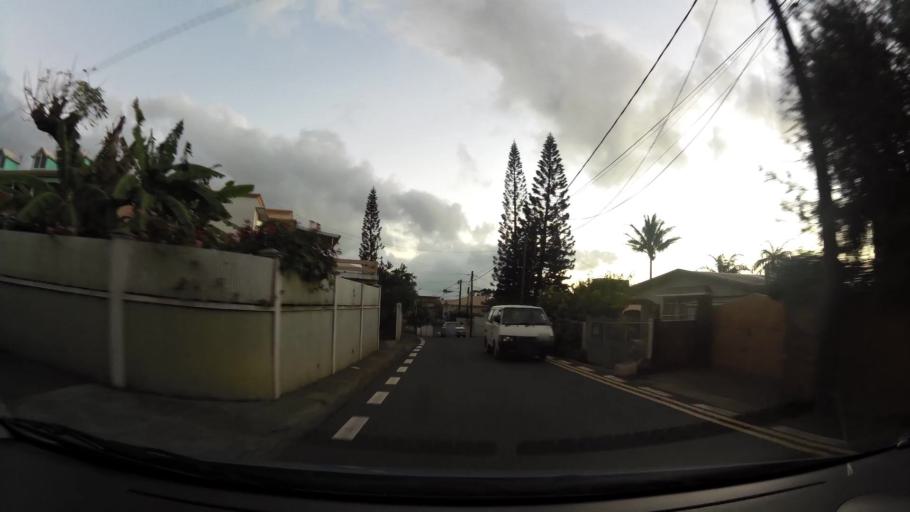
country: MU
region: Plaines Wilhems
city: Curepipe
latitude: -20.2913
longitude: 57.5218
